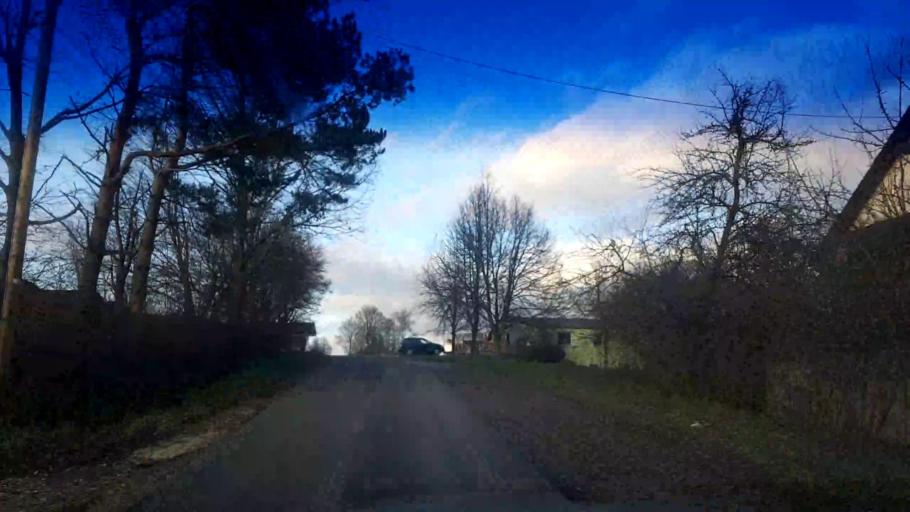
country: DE
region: Bavaria
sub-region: Upper Franconia
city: Buttenheim
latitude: 49.8090
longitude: 11.0397
